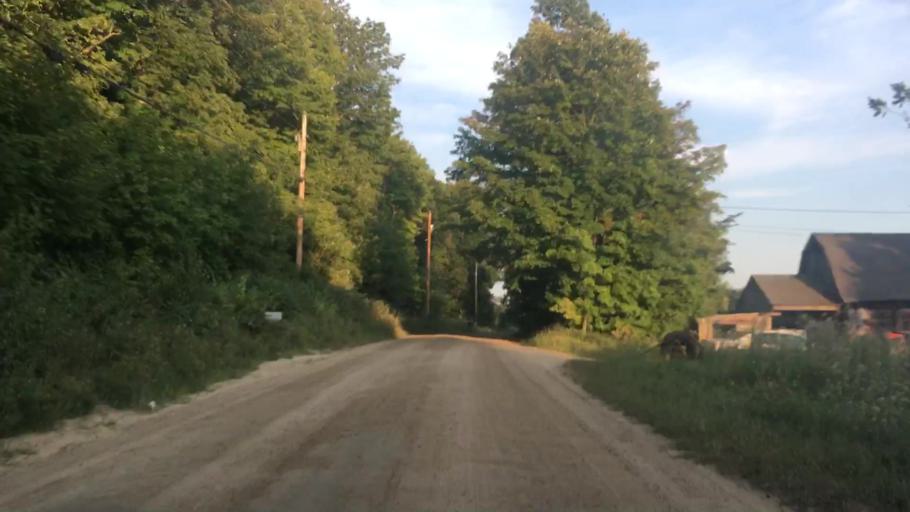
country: US
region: New Hampshire
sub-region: Belknap County
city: Barnstead
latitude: 43.4068
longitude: -71.2686
